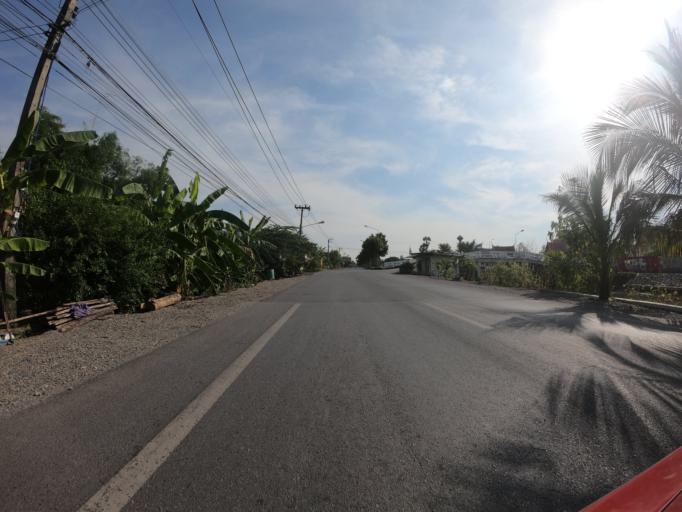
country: TH
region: Pathum Thani
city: Thanyaburi
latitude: 13.9817
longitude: 100.7292
